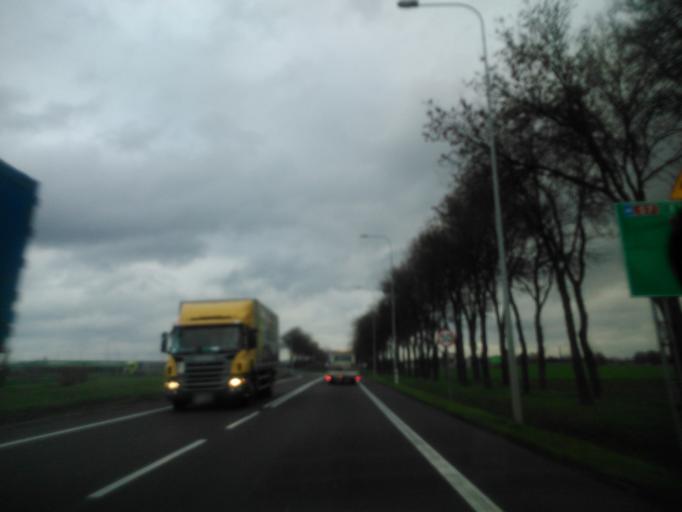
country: PL
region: Masovian Voivodeship
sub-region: Powiat plonski
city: Plonsk
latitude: 52.6050
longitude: 20.3930
